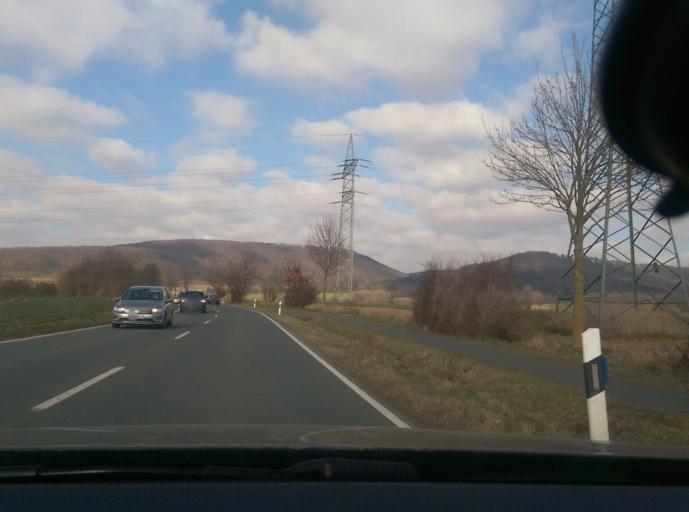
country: DE
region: Lower Saxony
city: Hessisch Oldendorf
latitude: 52.1803
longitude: 9.2540
